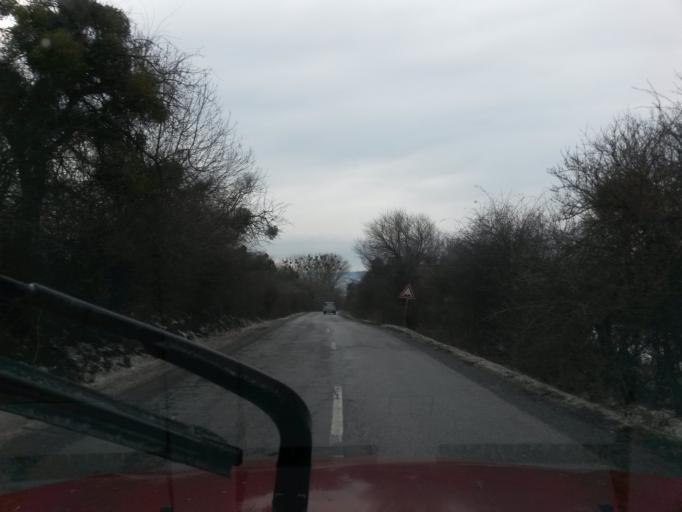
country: SK
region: Kosicky
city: Kosice
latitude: 48.7639
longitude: 21.3614
